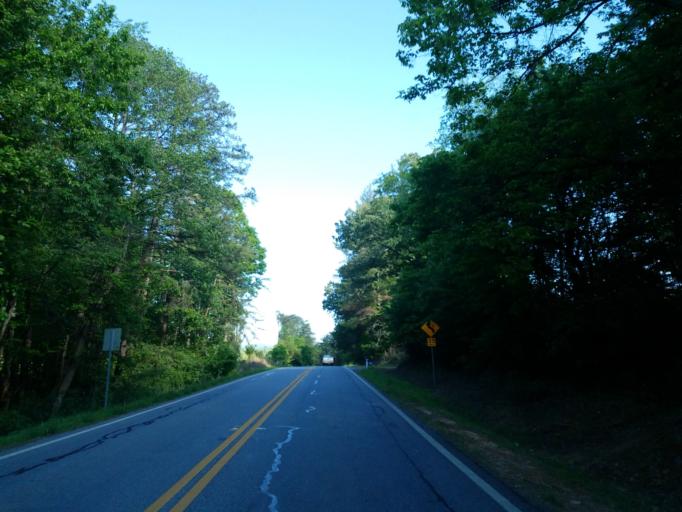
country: US
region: Georgia
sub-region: Fannin County
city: Blue Ridge
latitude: 34.8692
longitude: -84.2359
